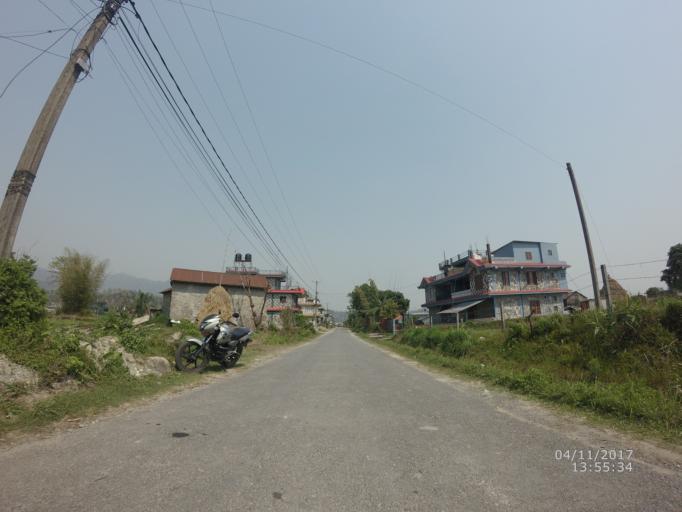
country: NP
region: Western Region
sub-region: Gandaki Zone
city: Pokhara
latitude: 28.1849
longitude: 84.0408
